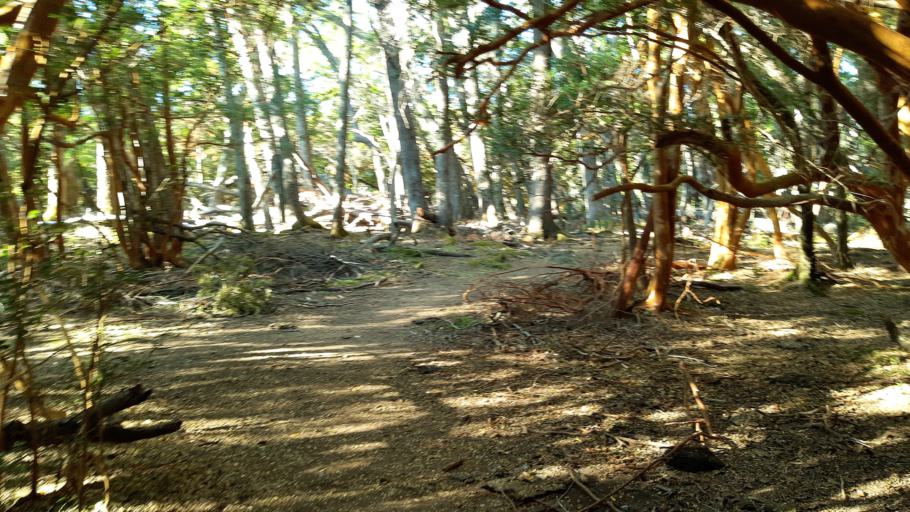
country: AR
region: Chubut
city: Trevelin
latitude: -42.7464
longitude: -71.7475
